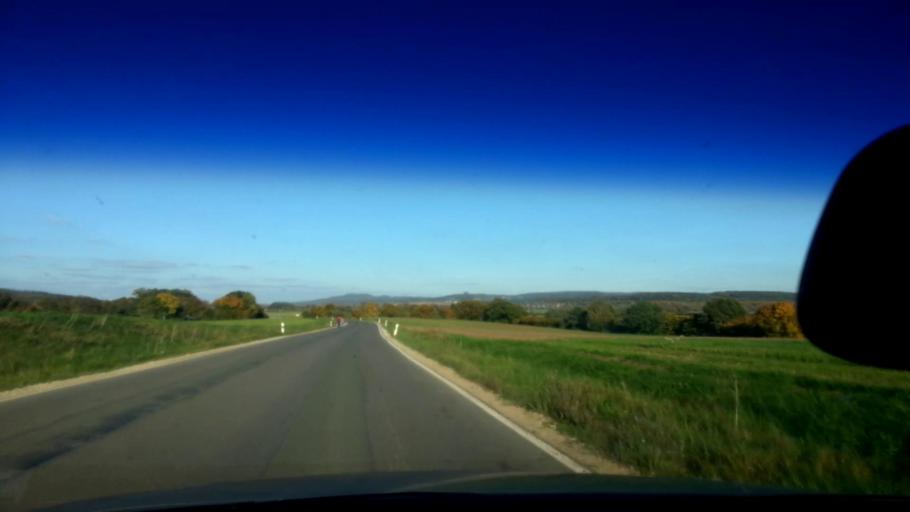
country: DE
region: Bavaria
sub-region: Upper Franconia
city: Rattelsdorf
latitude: 50.0220
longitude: 10.9032
